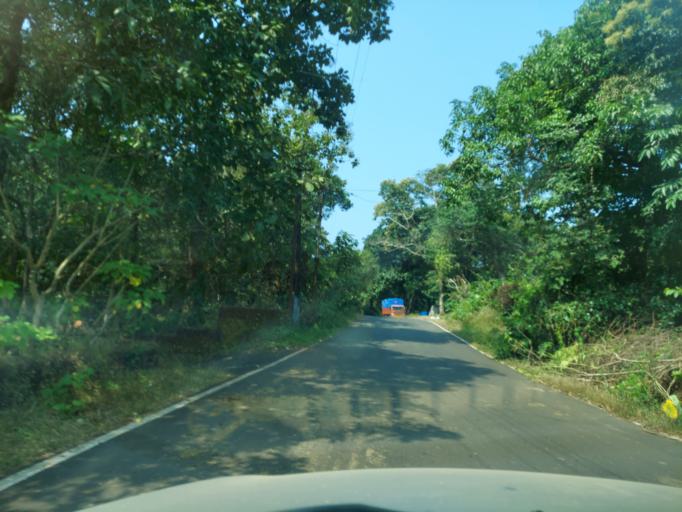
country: IN
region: Maharashtra
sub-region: Sindhudurg
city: Malvan
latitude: 15.9885
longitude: 73.5286
